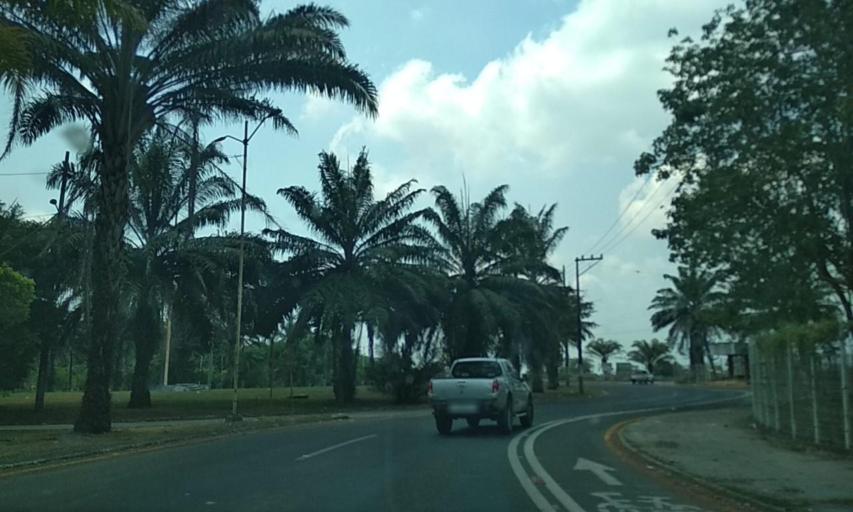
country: MX
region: Veracruz
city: Las Choapas
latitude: 17.9247
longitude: -94.0935
